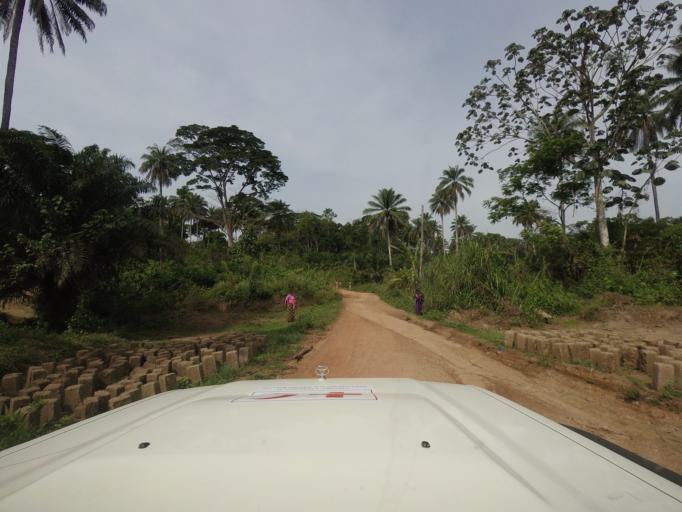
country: GN
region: Nzerekore
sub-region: Macenta
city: Macenta
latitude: 8.4791
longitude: -9.5516
